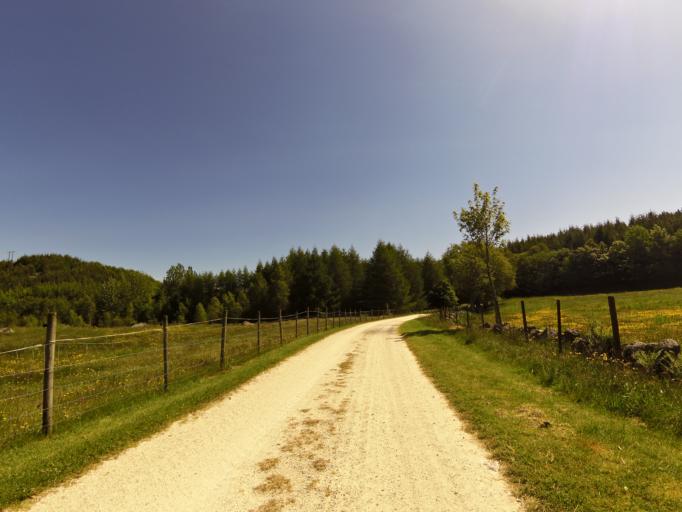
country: NO
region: Rogaland
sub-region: Eigersund
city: Egersund
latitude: 58.5031
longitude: 5.9065
